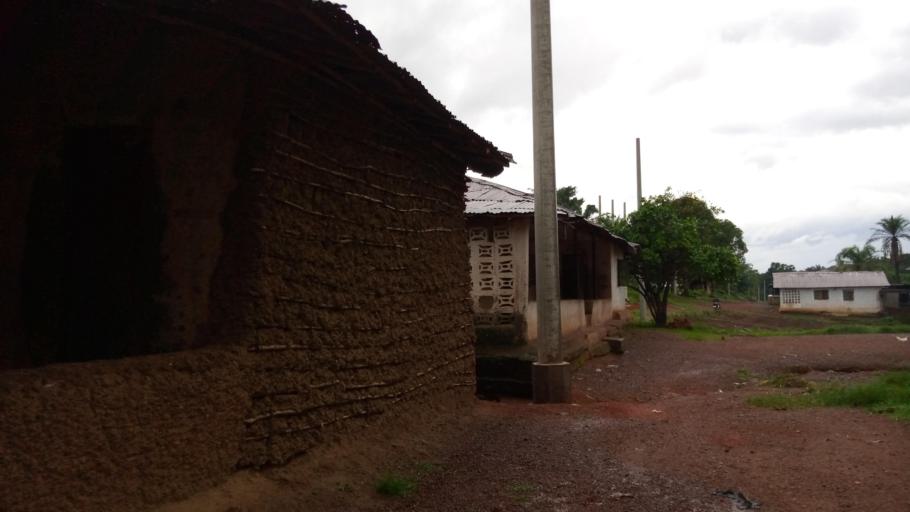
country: SL
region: Southern Province
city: Moyamba
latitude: 8.1639
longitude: -12.4366
